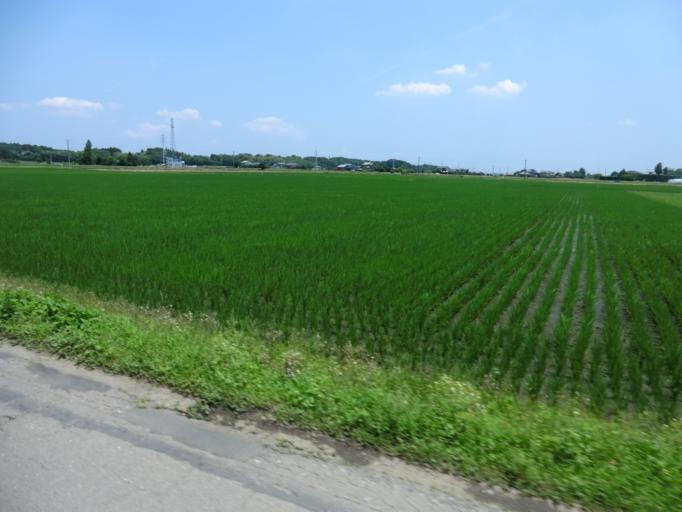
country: JP
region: Ibaraki
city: Moriya
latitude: 35.9656
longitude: 140.0493
